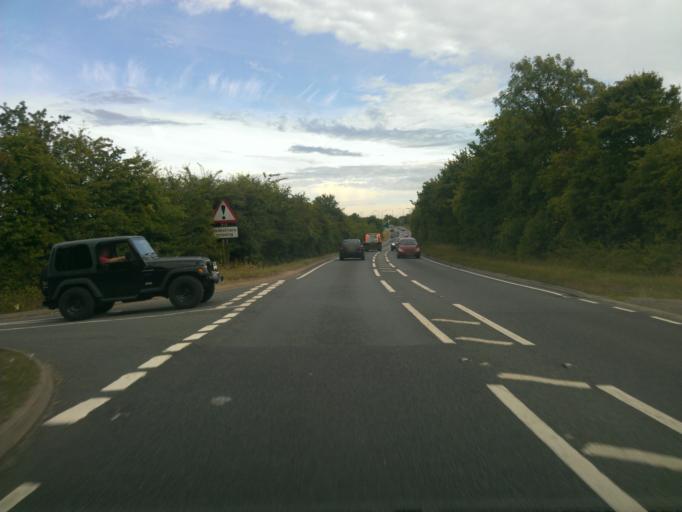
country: GB
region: England
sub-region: Essex
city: Coggeshall
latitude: 51.8777
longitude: 0.6989
